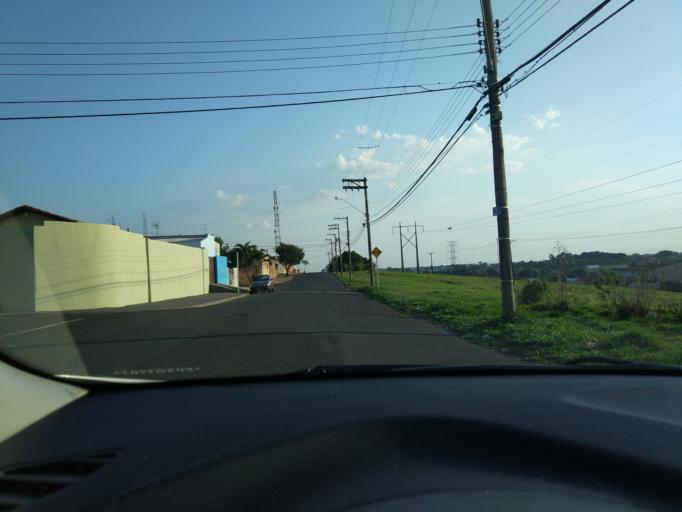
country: BR
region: Sao Paulo
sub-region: Botucatu
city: Botucatu
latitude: -22.9020
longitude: -48.4277
